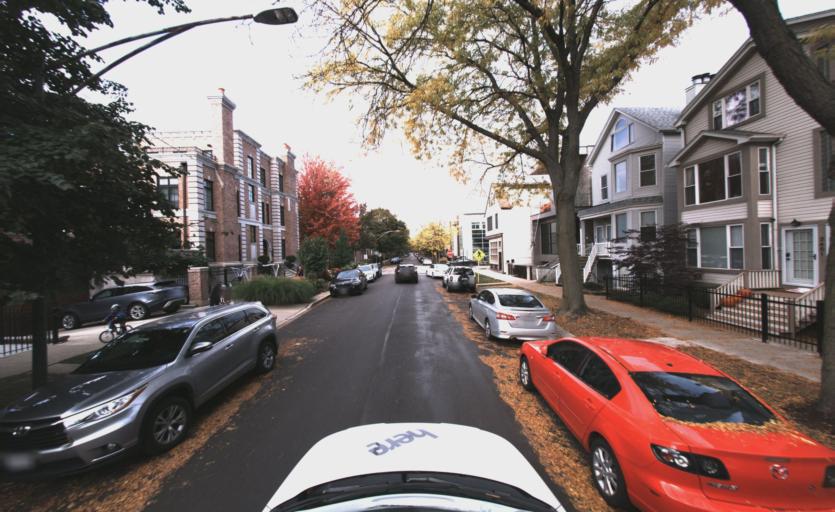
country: US
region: Illinois
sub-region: Cook County
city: Chicago
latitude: 41.9266
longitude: -87.6658
